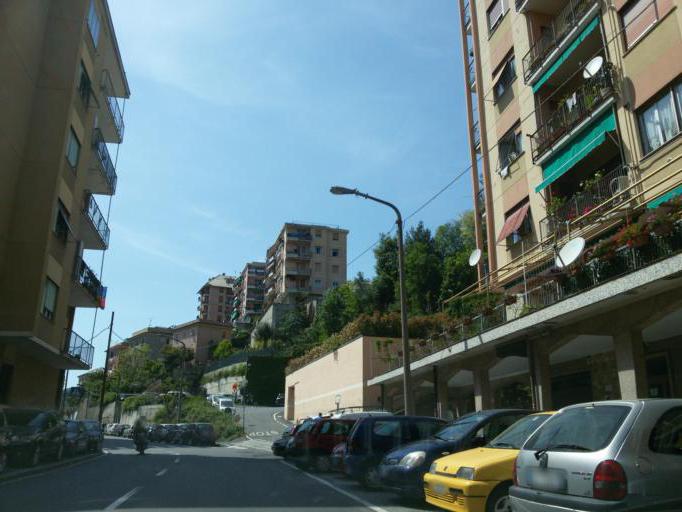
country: IT
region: Liguria
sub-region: Provincia di Genova
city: Genoa
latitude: 44.4189
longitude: 8.9615
